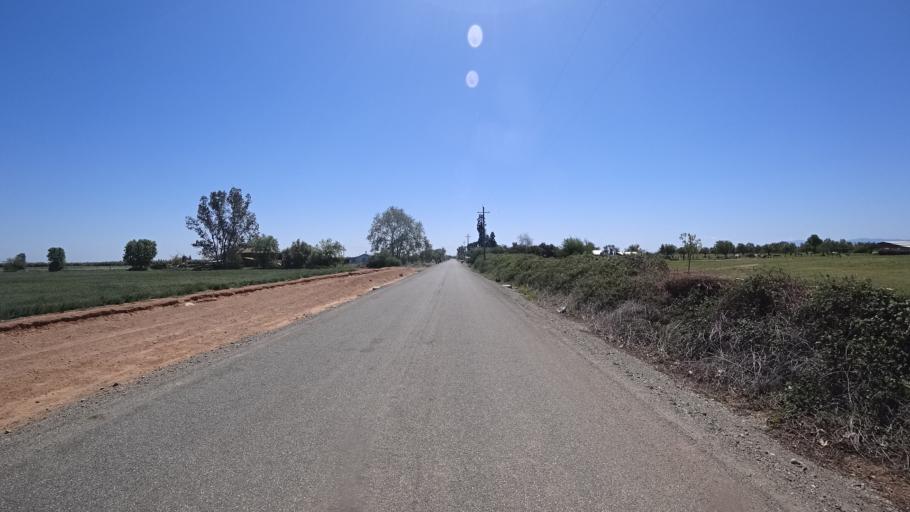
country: US
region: California
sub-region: Glenn County
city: Orland
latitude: 39.7934
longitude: -122.1784
